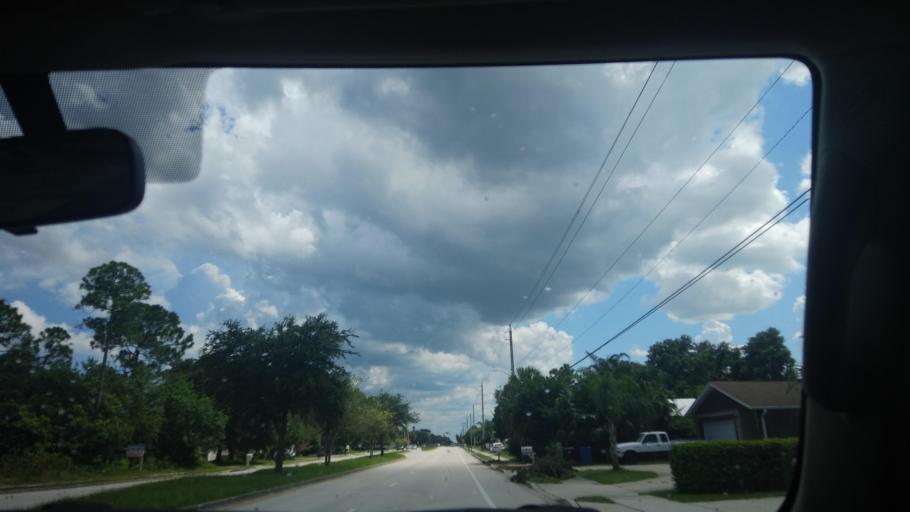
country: US
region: Florida
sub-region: Brevard County
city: Palm Bay
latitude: 27.9906
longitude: -80.6486
